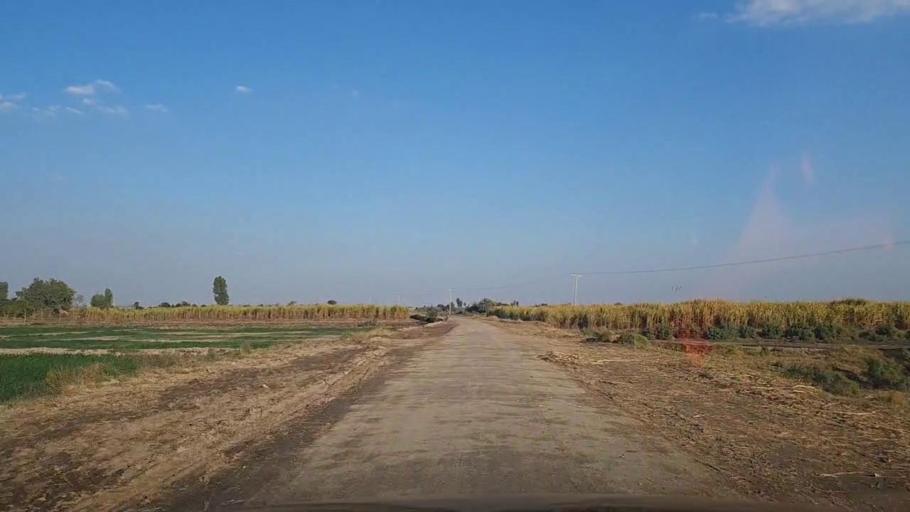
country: PK
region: Sindh
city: Sanghar
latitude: 25.9188
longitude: 69.0438
